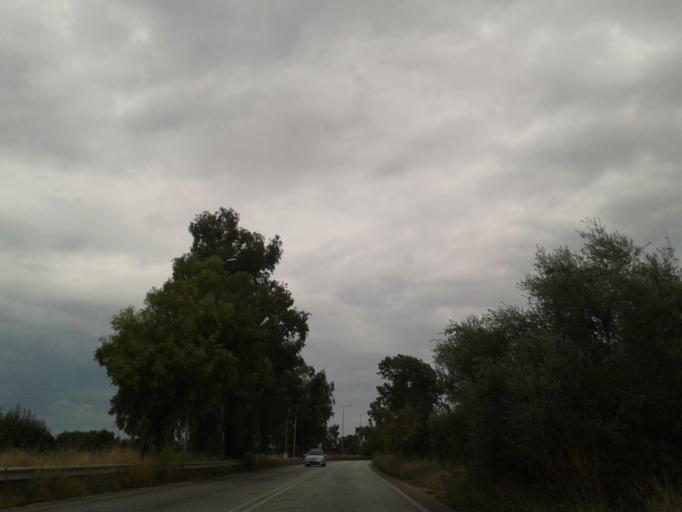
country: GR
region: Peloponnese
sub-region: Nomos Argolidos
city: Koutsopodi
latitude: 37.6681
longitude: 22.7225
